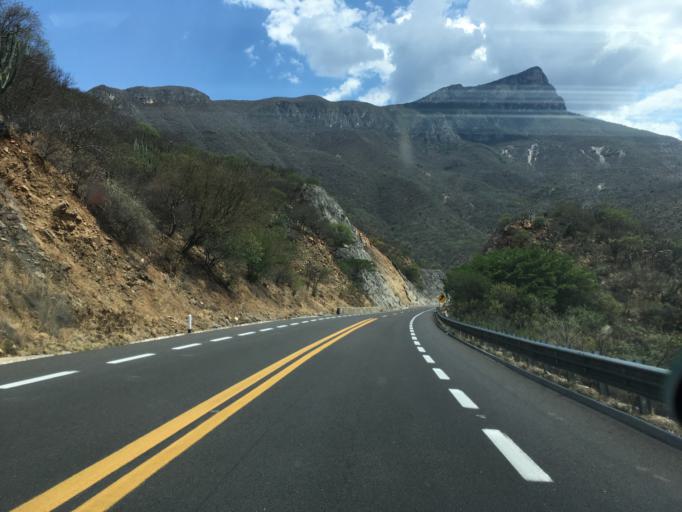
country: MX
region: Puebla
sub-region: San Jose Miahuatlan
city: San Pedro Tetitlan
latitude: 18.1496
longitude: -97.3059
